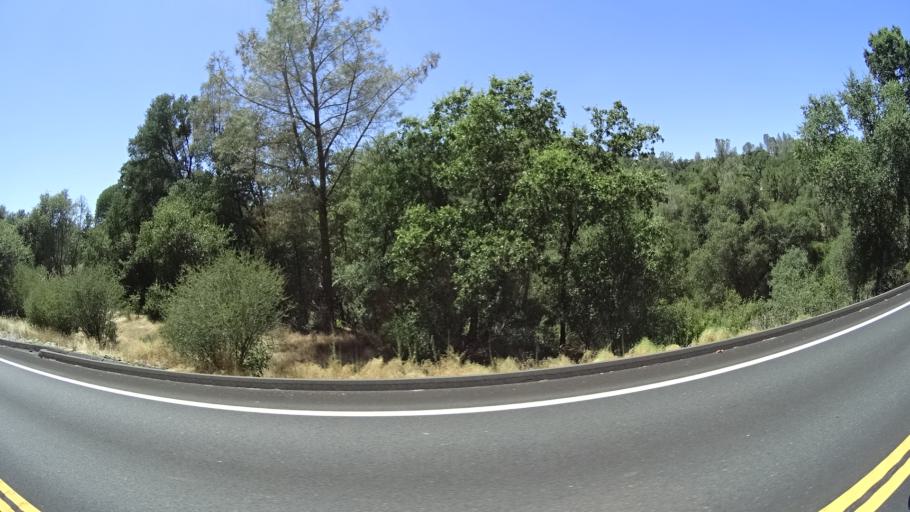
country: US
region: California
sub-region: Calaveras County
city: San Andreas
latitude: 38.2483
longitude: -120.7193
